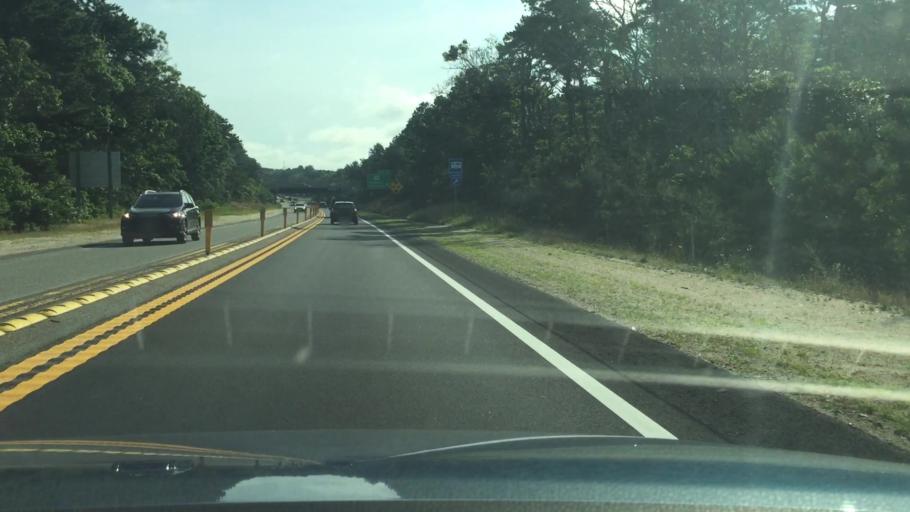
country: US
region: Massachusetts
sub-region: Barnstable County
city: East Harwich
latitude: 41.7211
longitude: -70.0375
